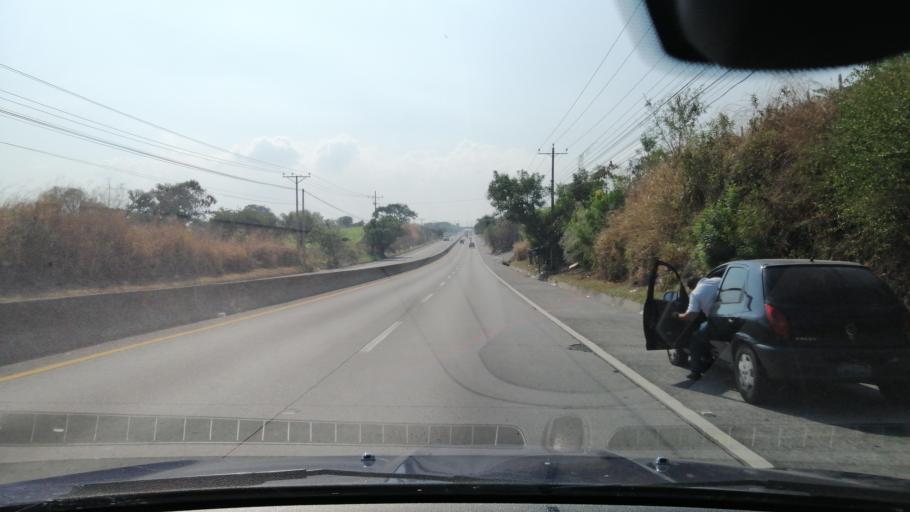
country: SV
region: San Salvador
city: Apopa
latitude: 13.7925
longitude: -89.2238
